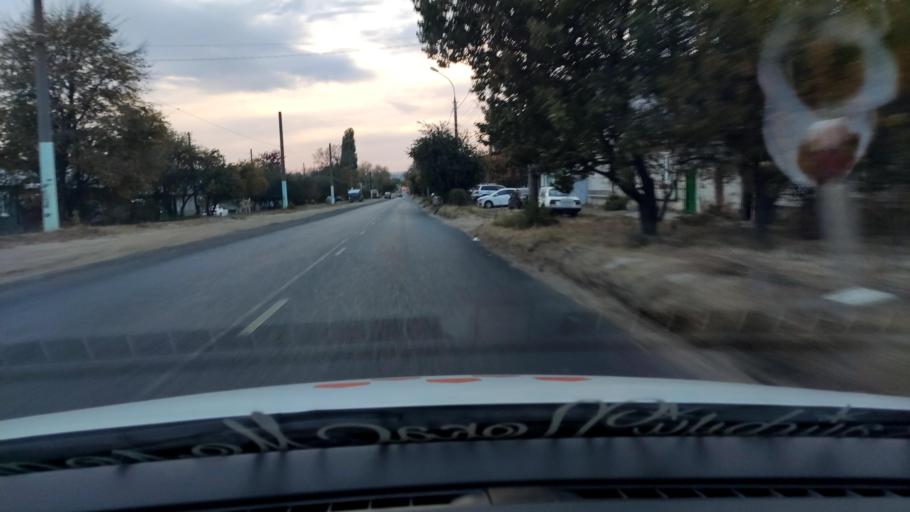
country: RU
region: Voronezj
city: Voronezh
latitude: 51.6978
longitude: 39.1735
